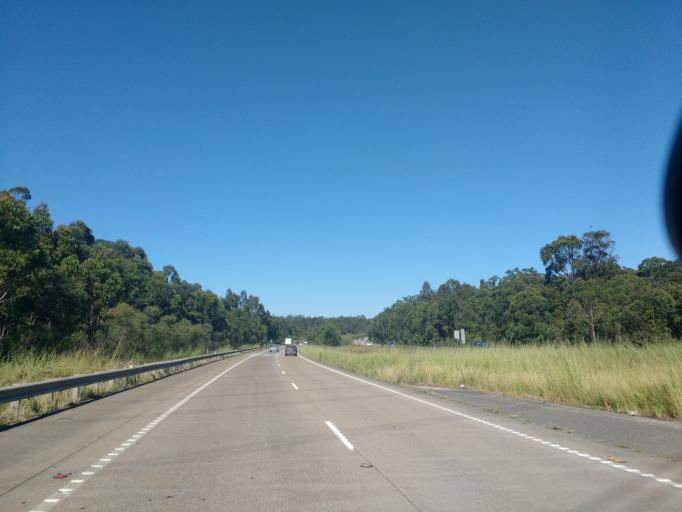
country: AU
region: New South Wales
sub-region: Lake Macquarie Shire
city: Holmesville
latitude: -32.9291
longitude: 151.5506
